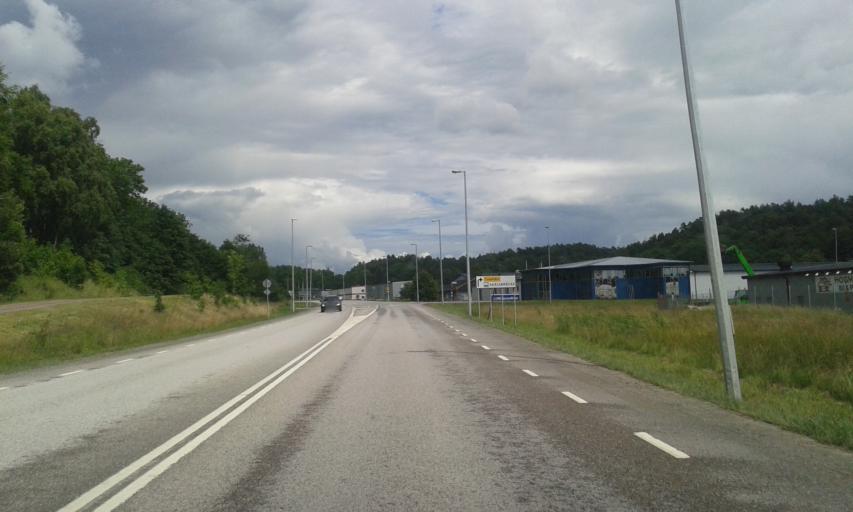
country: SE
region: Vaestra Goetaland
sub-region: Kungalvs Kommun
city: Kungalv
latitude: 57.8862
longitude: 11.9848
